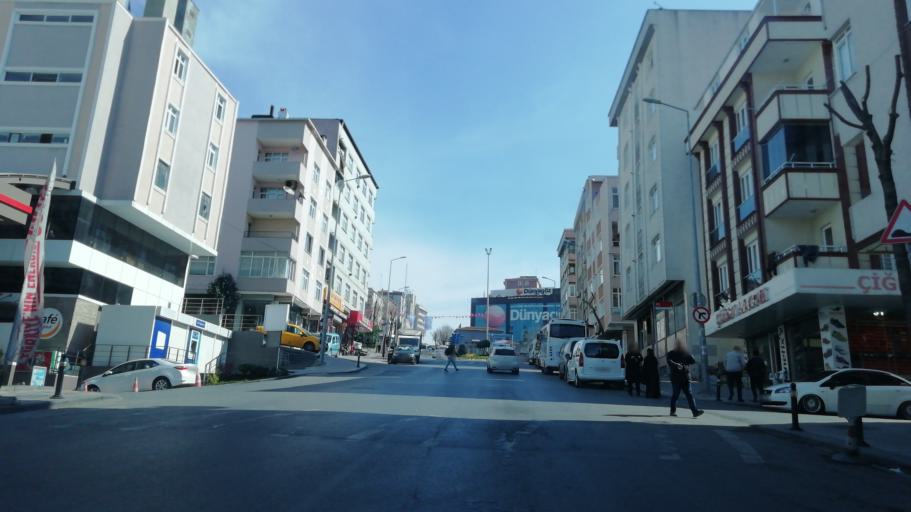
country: TR
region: Istanbul
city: Bagcilar
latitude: 41.0332
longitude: 28.8512
